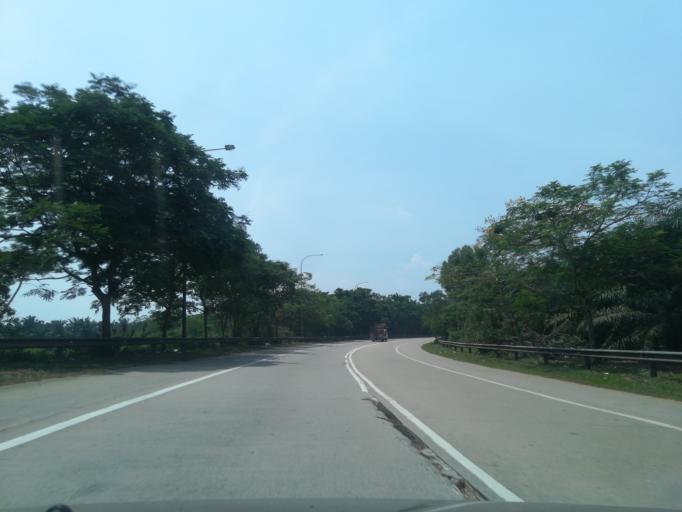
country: MY
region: Kedah
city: Kulim
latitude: 5.4279
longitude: 100.5621
